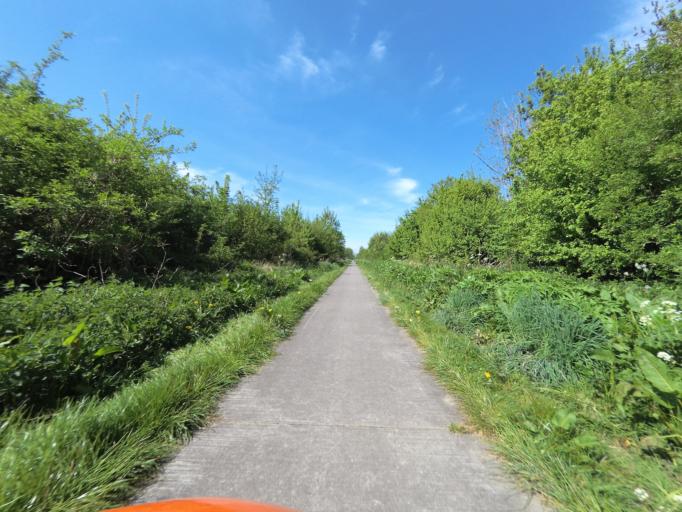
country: NL
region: Flevoland
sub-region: Gemeente Dronten
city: Dronten
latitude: 52.5213
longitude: 5.6735
